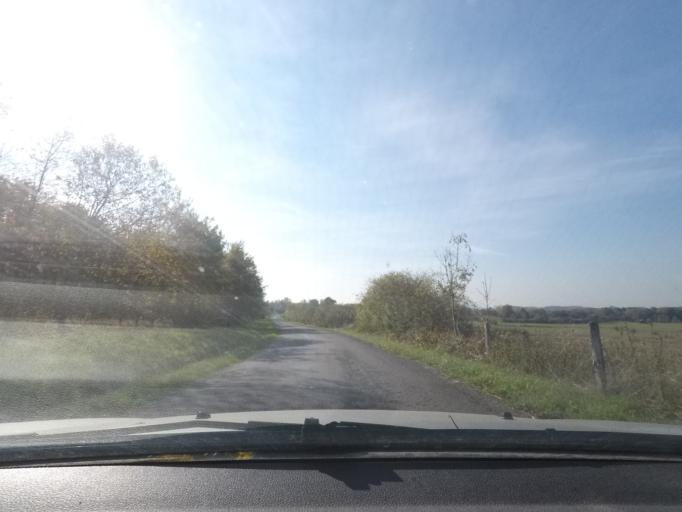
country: BE
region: Wallonia
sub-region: Province du Luxembourg
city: Tintigny
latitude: 49.7027
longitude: 5.5033
